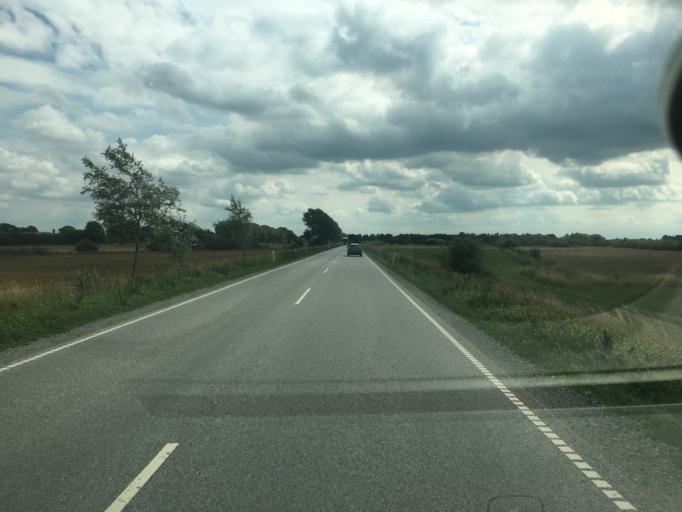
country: DK
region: South Denmark
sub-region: Aabenraa Kommune
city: Tinglev
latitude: 54.9809
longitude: 9.2935
